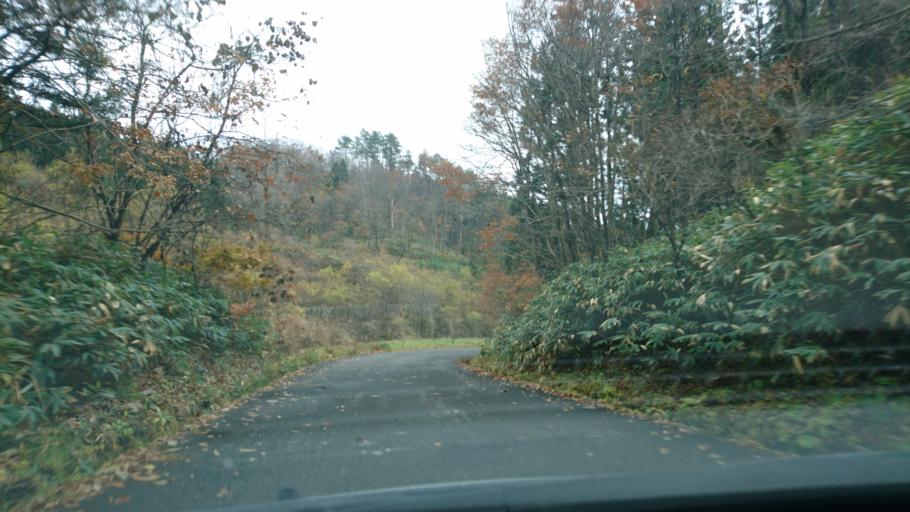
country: JP
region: Iwate
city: Ichinoseki
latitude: 38.9150
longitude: 140.9068
